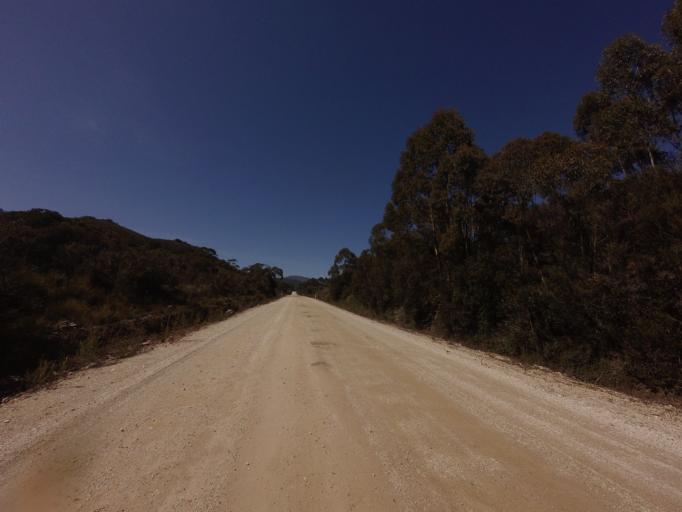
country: AU
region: Tasmania
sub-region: Huon Valley
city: Geeveston
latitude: -42.9454
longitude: 146.3507
